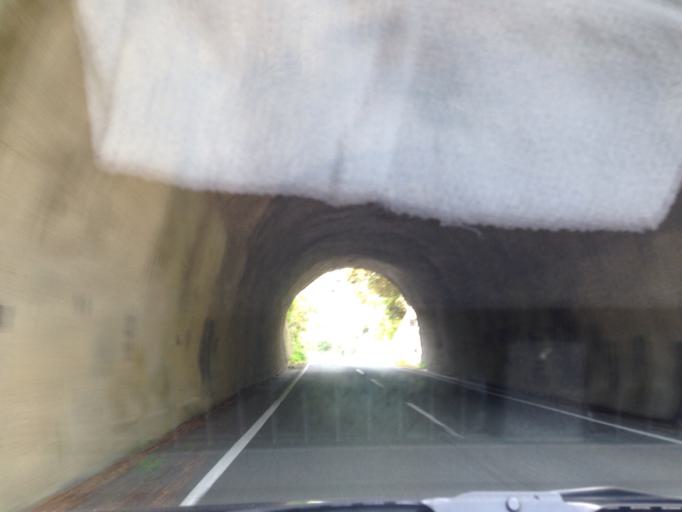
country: JP
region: Shizuoka
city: Shimoda
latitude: 34.6332
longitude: 138.8166
